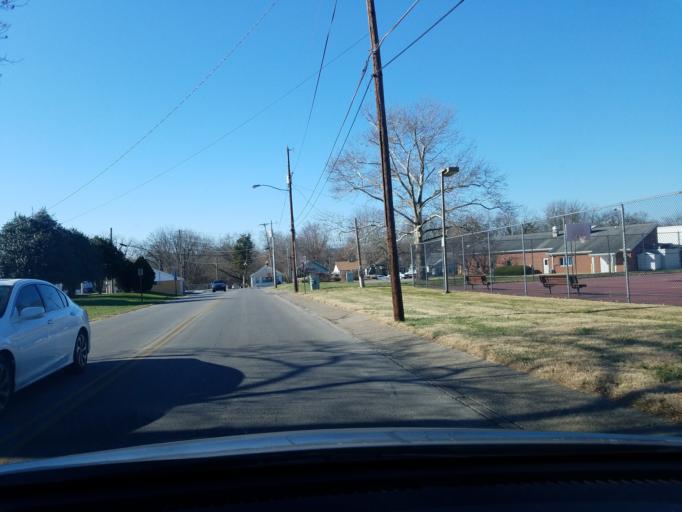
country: US
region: Indiana
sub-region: Floyd County
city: New Albany
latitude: 38.2959
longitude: -85.8256
